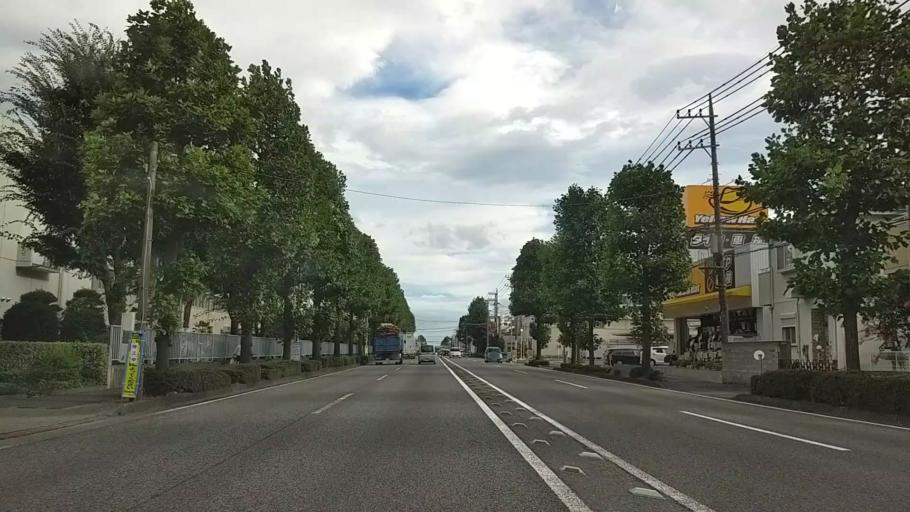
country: JP
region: Tokyo
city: Hachioji
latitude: 35.5834
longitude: 139.3457
